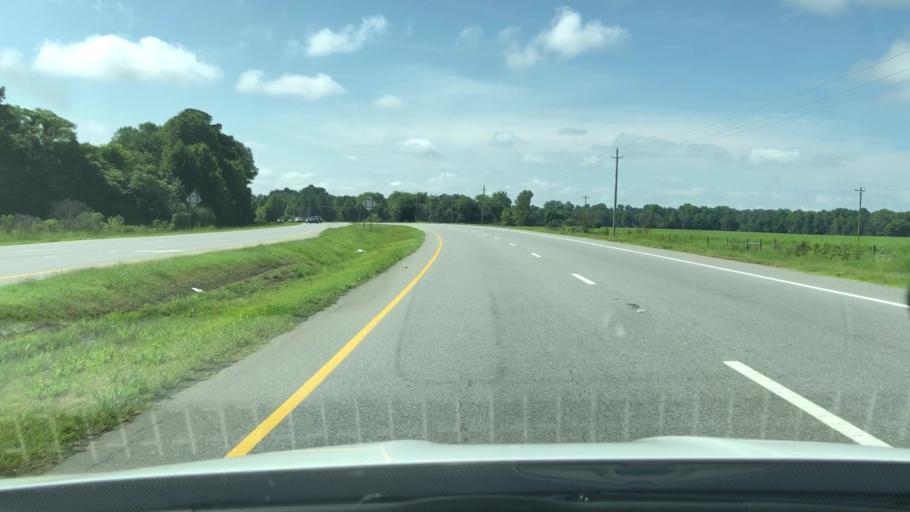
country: US
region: North Carolina
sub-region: Bertie County
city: Windsor
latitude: 35.9947
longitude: -76.9651
